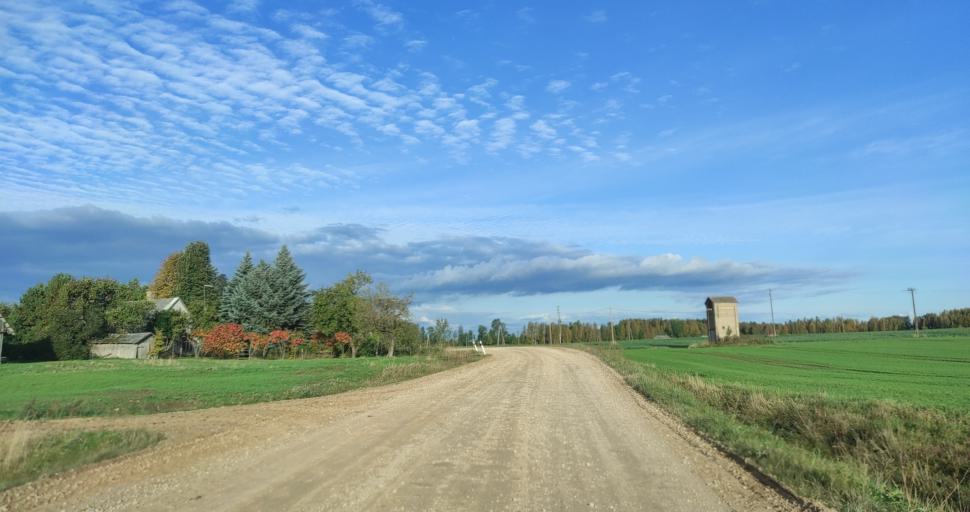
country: LV
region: Skrunda
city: Skrunda
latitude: 56.7455
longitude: 21.8369
